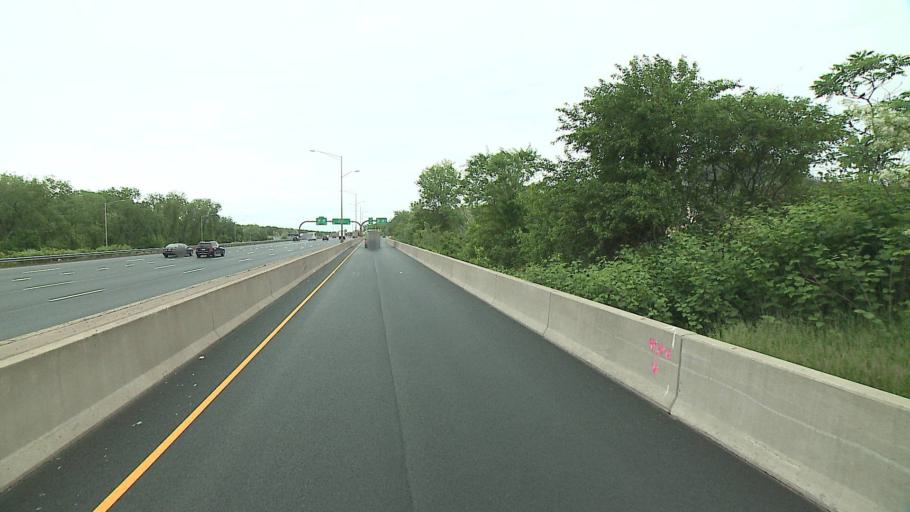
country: US
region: Connecticut
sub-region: Hartford County
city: Plainville
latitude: 41.6691
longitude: -72.8329
